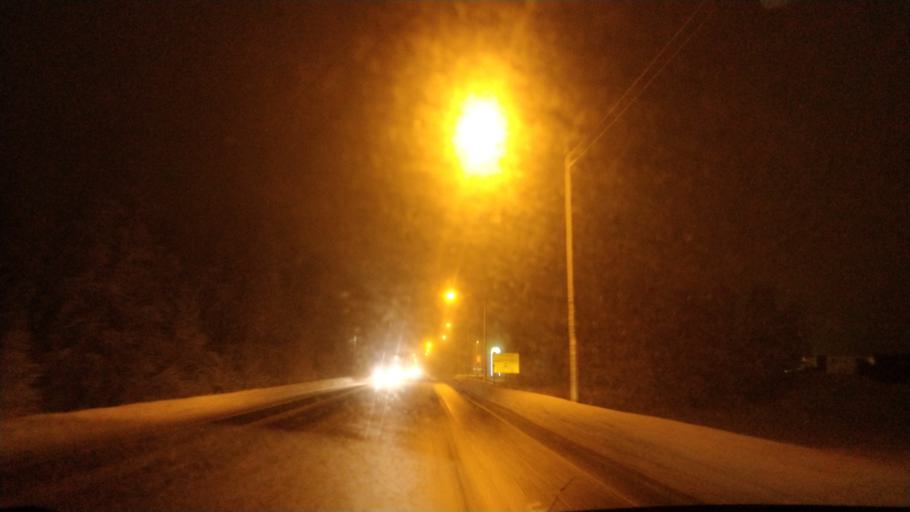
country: FI
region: Lapland
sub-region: Rovaniemi
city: Rovaniemi
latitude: 66.4794
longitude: 25.6267
